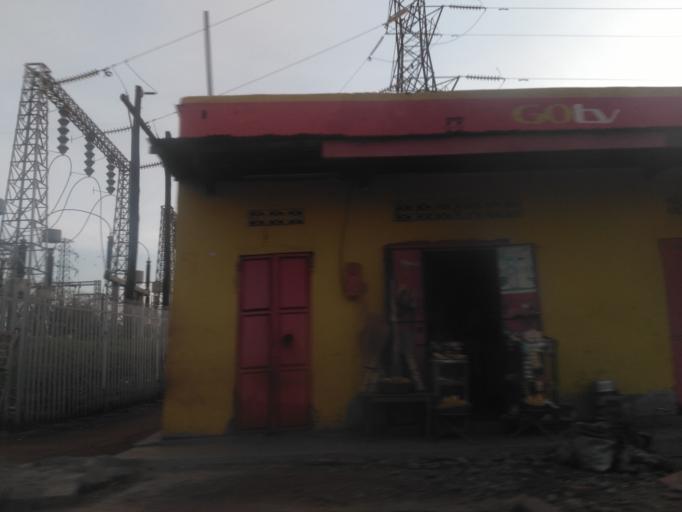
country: UG
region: Central Region
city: Kampala Central Division
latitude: 0.3475
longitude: 32.5747
